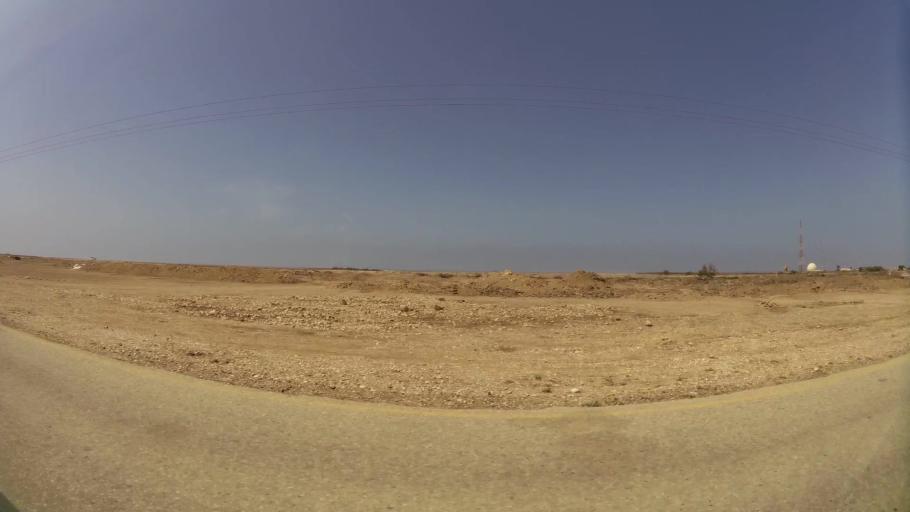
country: OM
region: Zufar
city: Salalah
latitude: 17.0373
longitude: 54.2643
